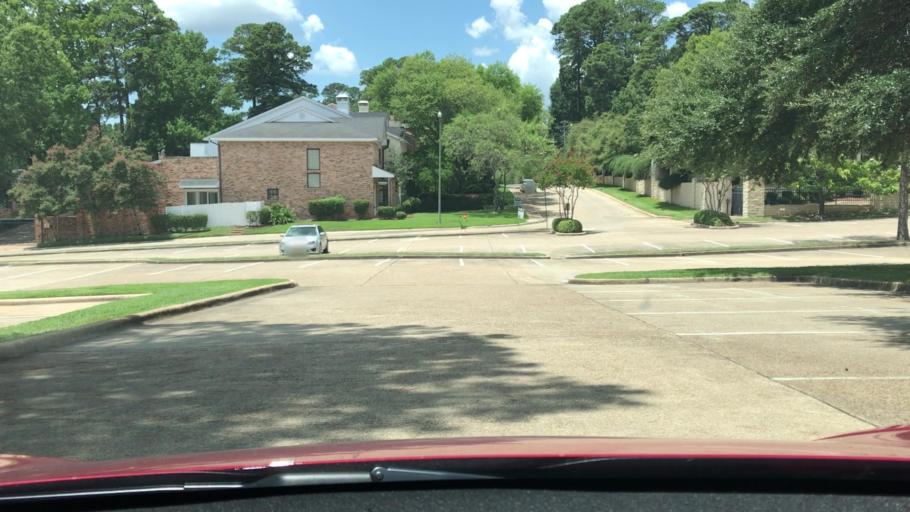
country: US
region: Louisiana
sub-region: Bossier Parish
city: Bossier City
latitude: 32.4564
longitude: -93.7487
